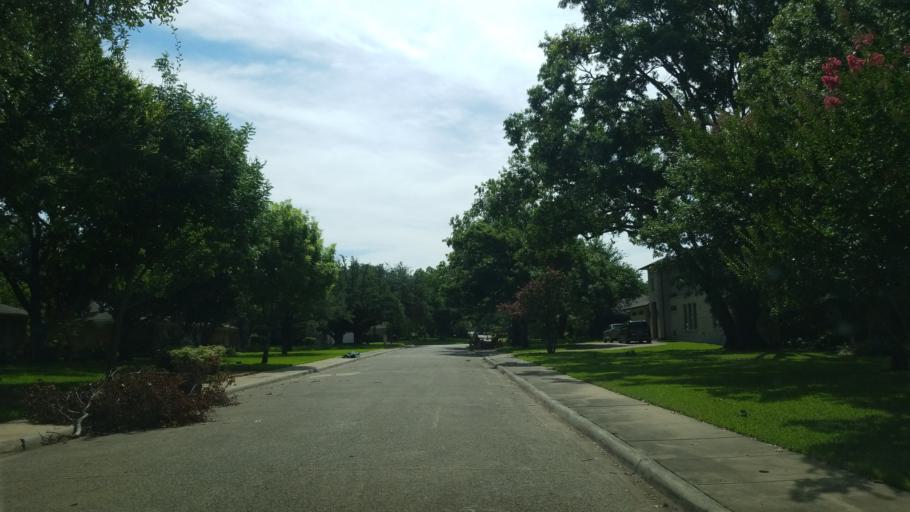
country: US
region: Texas
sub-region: Dallas County
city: Farmers Branch
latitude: 32.9051
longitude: -96.8448
